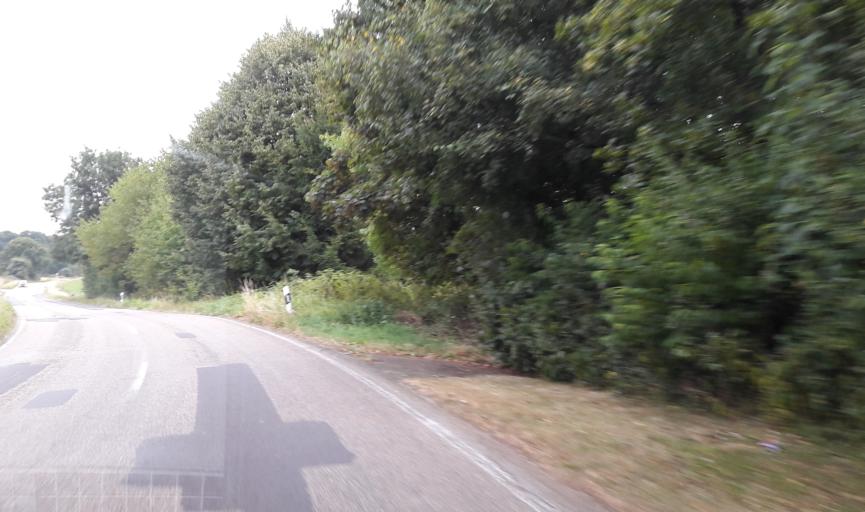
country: DE
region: Saarland
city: Tholey
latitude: 49.4749
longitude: 7.0365
